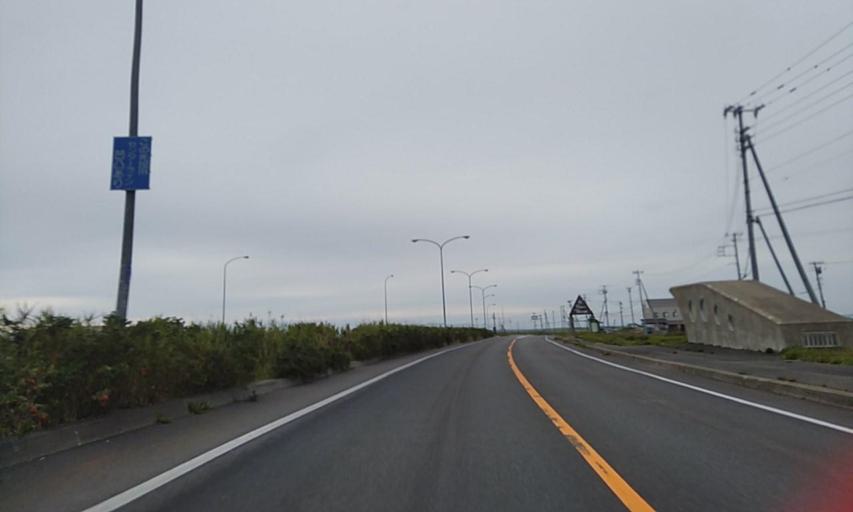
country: JP
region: Hokkaido
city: Makubetsu
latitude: 45.3309
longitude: 142.1771
